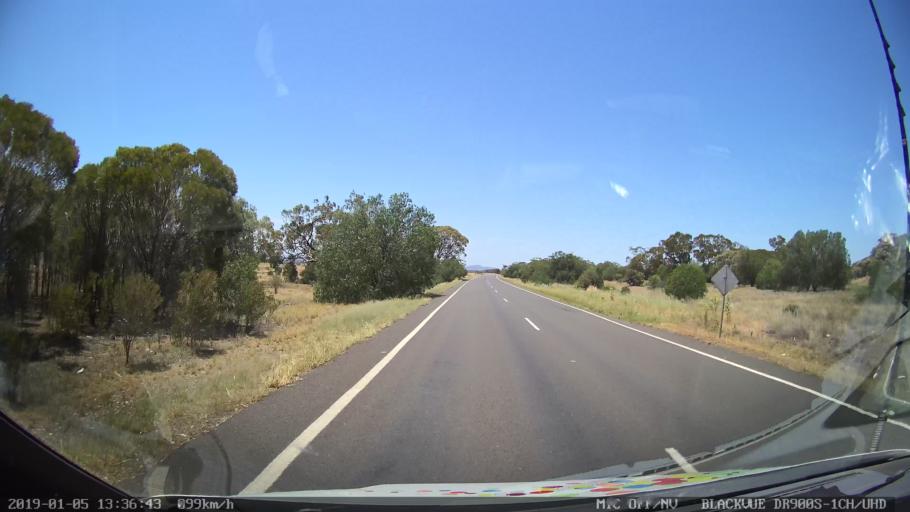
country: AU
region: New South Wales
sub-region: Gunnedah
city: Gunnedah
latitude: -30.9834
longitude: 150.1690
